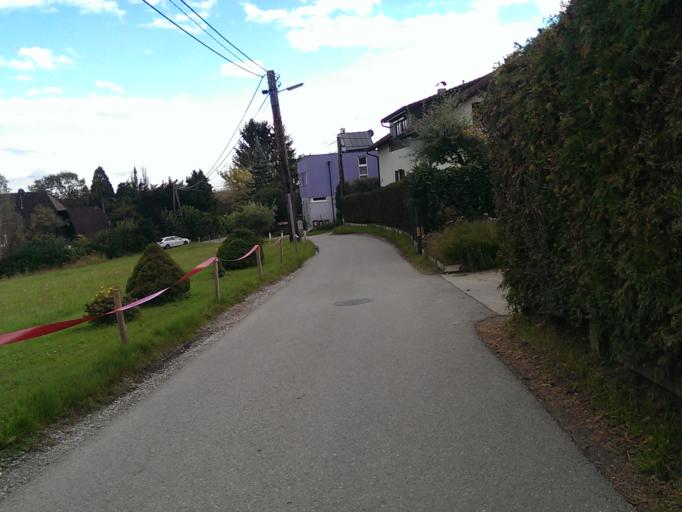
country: AT
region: Styria
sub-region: Politischer Bezirk Graz-Umgebung
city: Raaba
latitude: 47.0451
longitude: 15.4915
